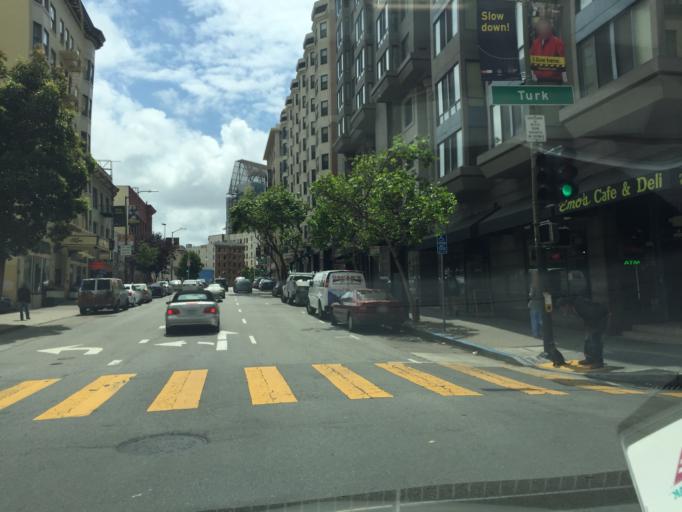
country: US
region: California
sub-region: San Francisco County
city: San Francisco
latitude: 37.7831
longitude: -122.4125
